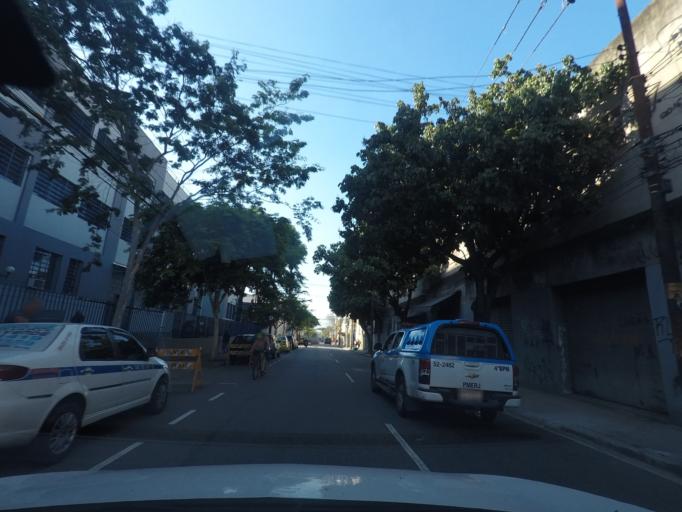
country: BR
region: Rio de Janeiro
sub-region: Rio De Janeiro
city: Rio de Janeiro
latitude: -22.8967
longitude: -43.2265
